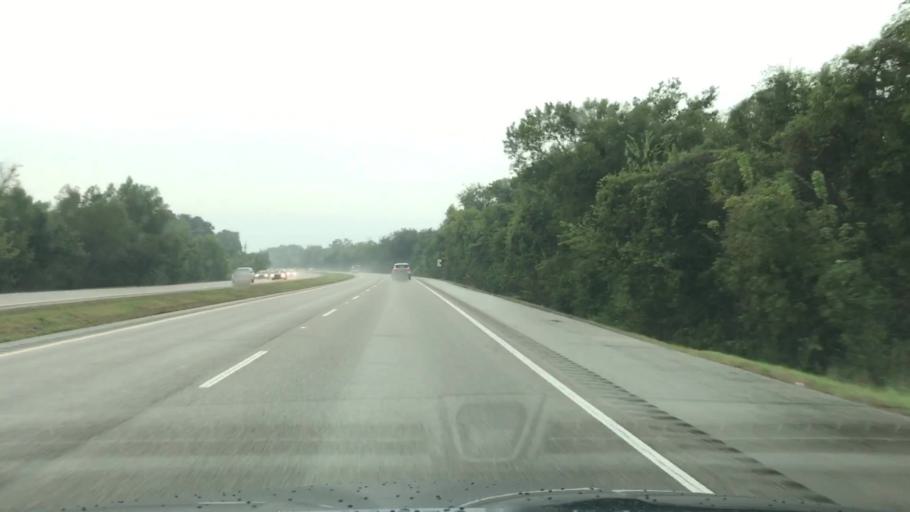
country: US
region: Louisiana
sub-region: Saint Charles Parish
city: Paradis
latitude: 29.8571
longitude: -90.4474
